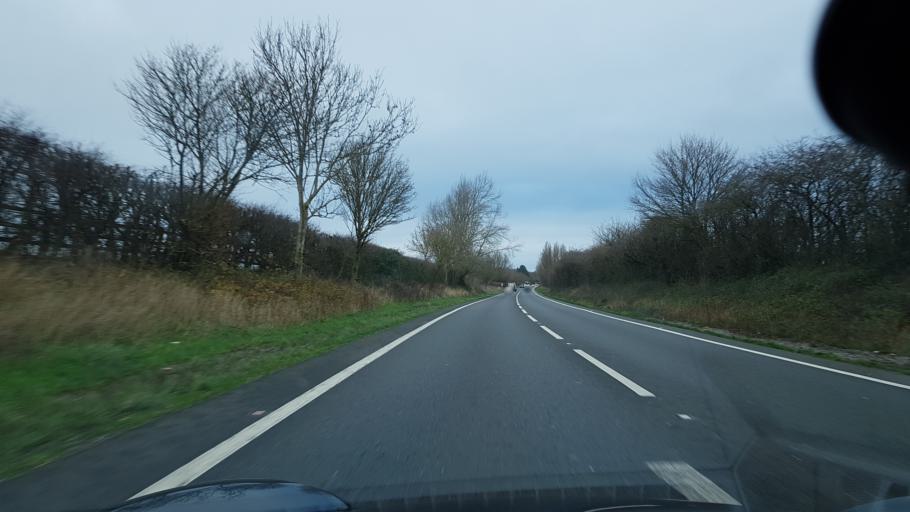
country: GB
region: England
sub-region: Somerset
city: Creech Saint Michael
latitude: 50.9663
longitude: -2.9994
